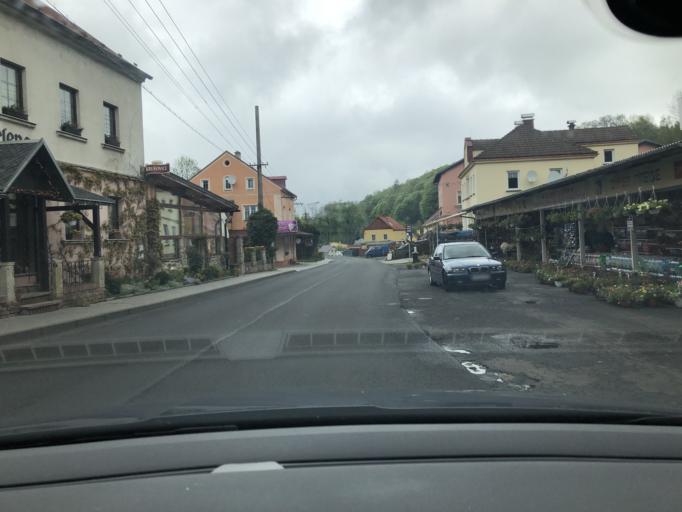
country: CZ
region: Ustecky
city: Libouchec
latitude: 50.7952
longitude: 13.9773
